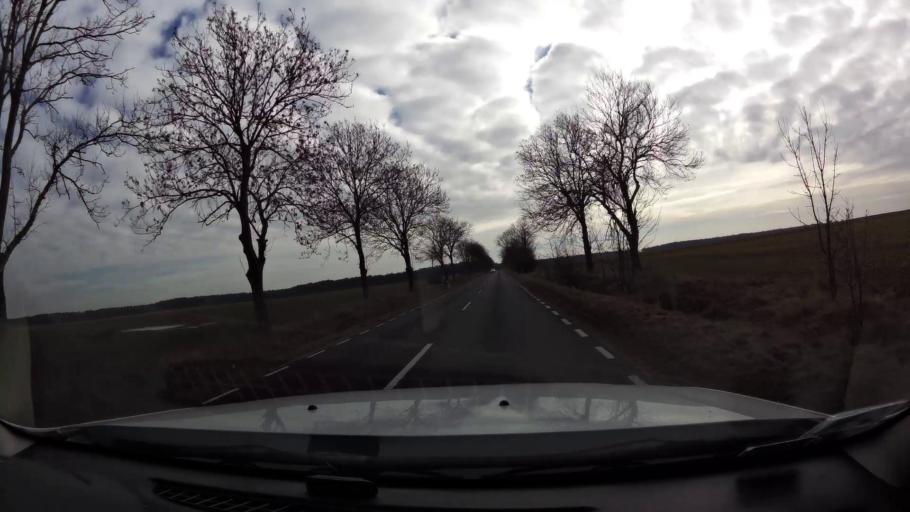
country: PL
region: West Pomeranian Voivodeship
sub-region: Powiat mysliborski
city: Debno
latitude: 52.7781
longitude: 14.6537
